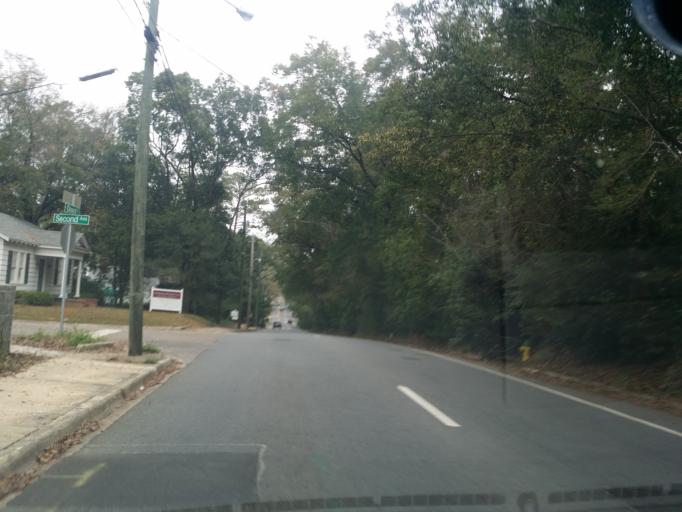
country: US
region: Florida
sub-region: Leon County
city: Tallahassee
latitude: 30.4512
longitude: -84.2832
